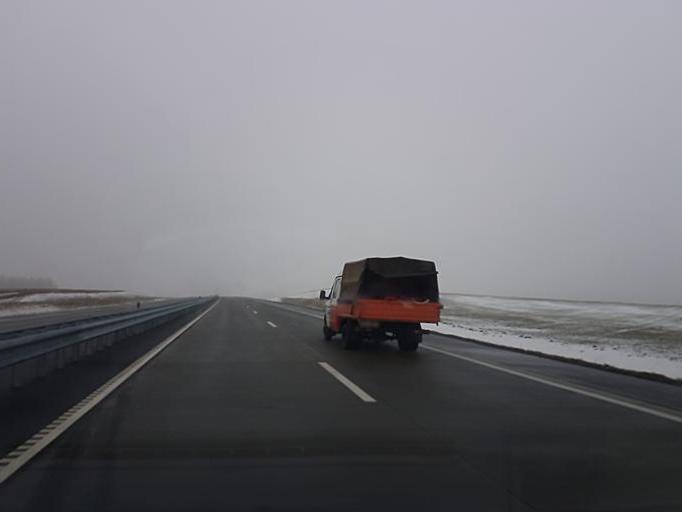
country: BY
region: Minsk
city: Atolina
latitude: 53.7495
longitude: 27.4131
